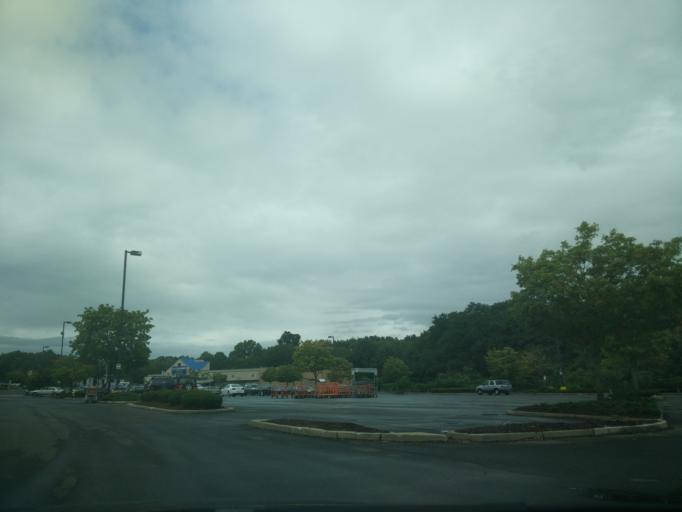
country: US
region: Connecticut
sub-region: New Haven County
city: Orange
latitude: 41.2563
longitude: -73.0105
